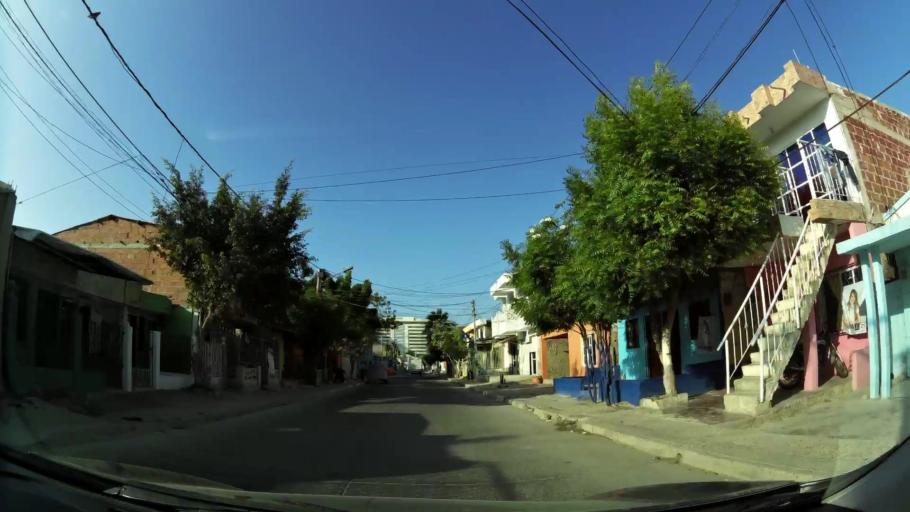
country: CO
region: Bolivar
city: Cartagena
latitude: 10.4396
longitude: -75.5255
